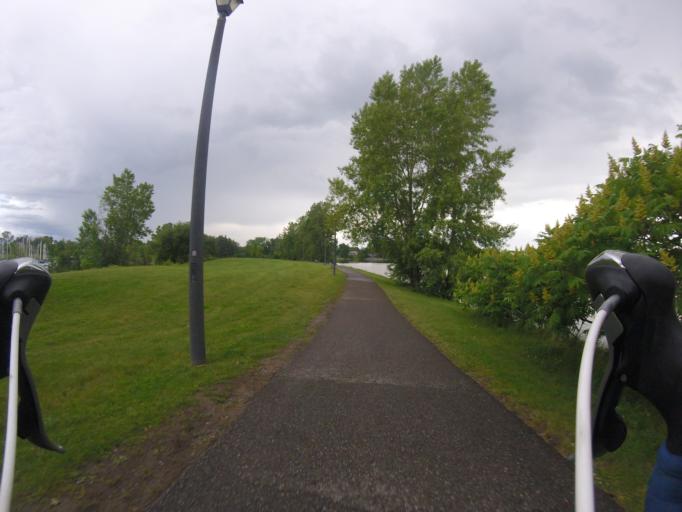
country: CA
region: Ontario
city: Bells Corners
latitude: 45.3541
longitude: -75.8269
